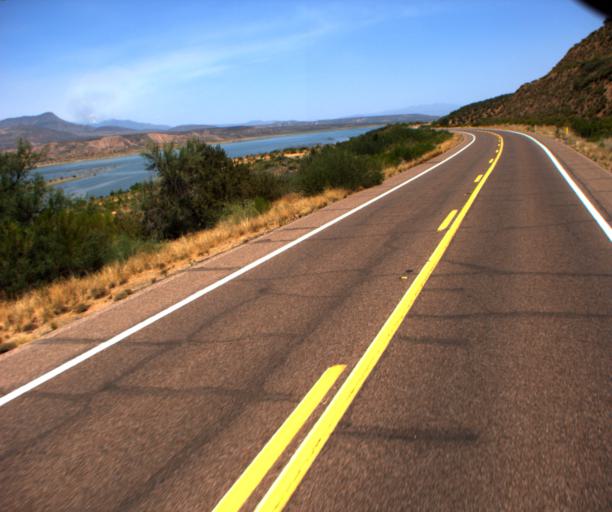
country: US
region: Arizona
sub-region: Gila County
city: Tonto Basin
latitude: 33.7531
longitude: -111.2422
